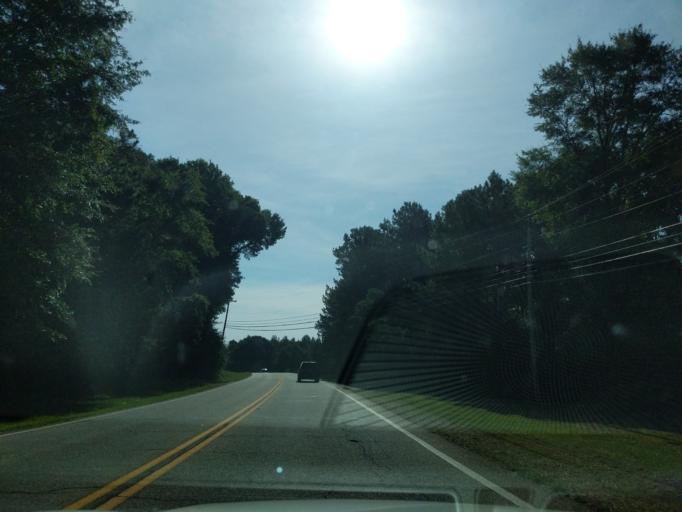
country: US
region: Georgia
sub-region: Troup County
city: Hogansville
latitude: 33.1637
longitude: -84.8828
